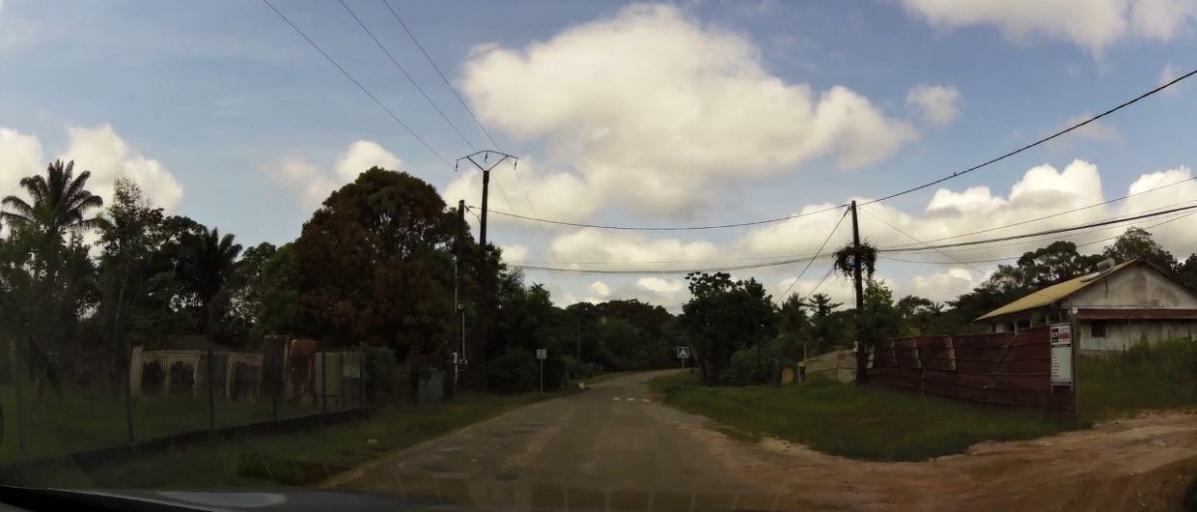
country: GF
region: Guyane
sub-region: Guyane
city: Matoury
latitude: 4.8310
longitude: -52.3105
